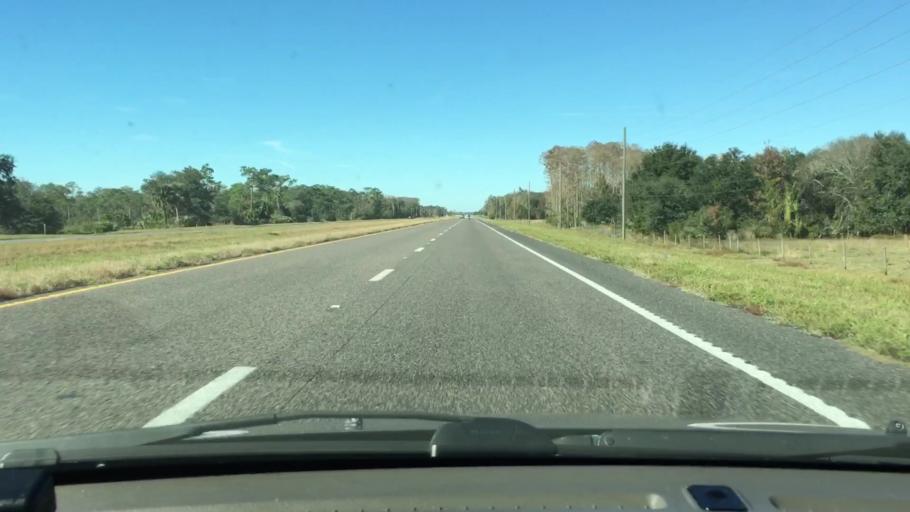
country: US
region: Florida
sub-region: Brevard County
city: June Park
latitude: 28.1222
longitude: -80.9558
